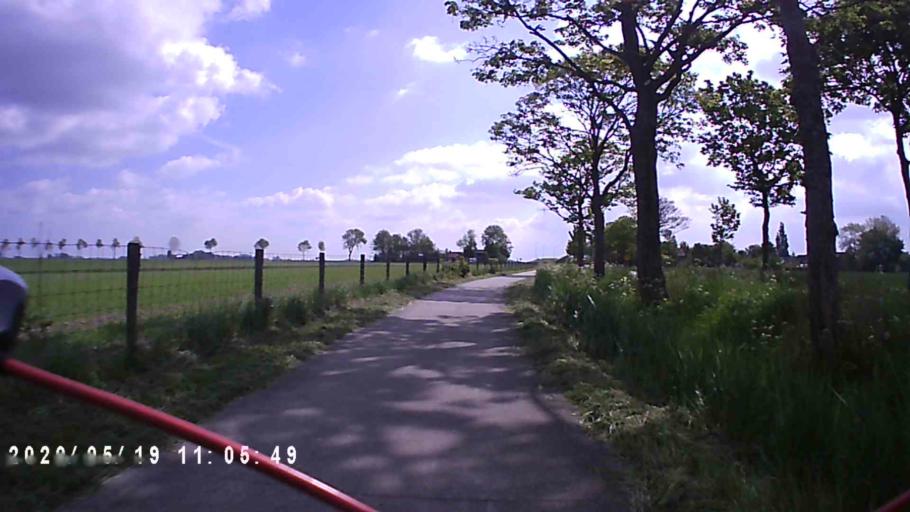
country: NL
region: Groningen
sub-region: Gemeente Zuidhorn
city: Grijpskerk
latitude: 53.2952
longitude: 6.2926
